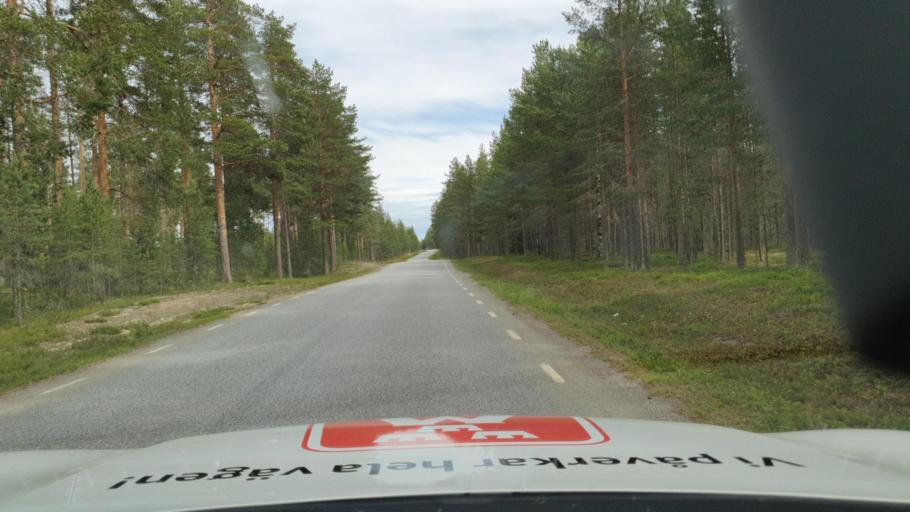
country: SE
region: Vaesterbotten
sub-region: Skelleftea Kommun
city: Burtraesk
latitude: 64.5051
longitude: 20.7757
